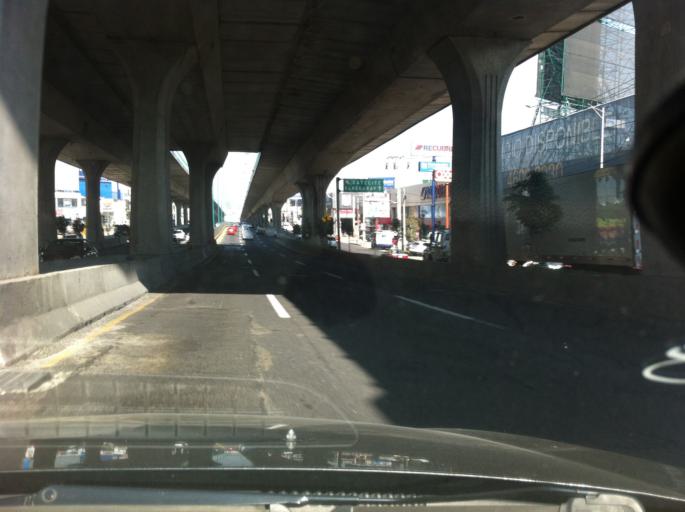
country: MX
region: Mexico
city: Naucalpan de Juarez
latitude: 19.4665
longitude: -99.2251
